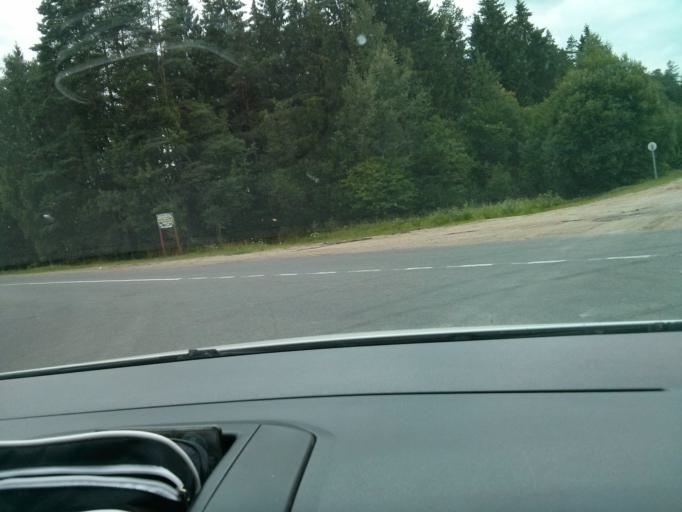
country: BY
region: Minsk
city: Horad Barysaw
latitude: 54.2908
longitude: 28.5278
